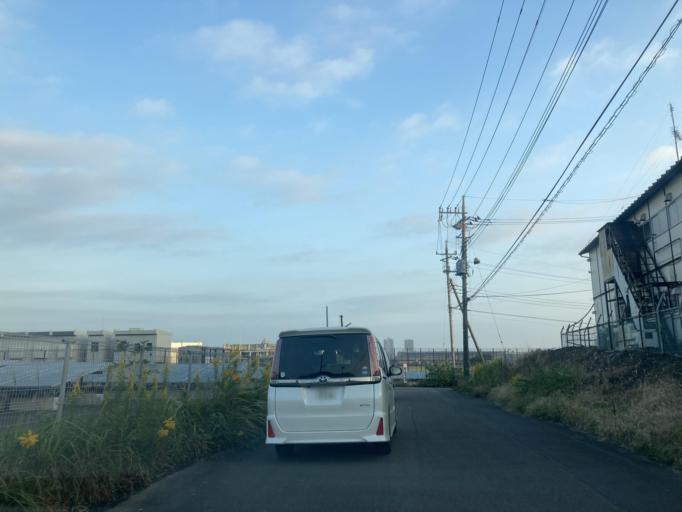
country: JP
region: Tokyo
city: Kokubunji
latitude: 35.6477
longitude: 139.4809
